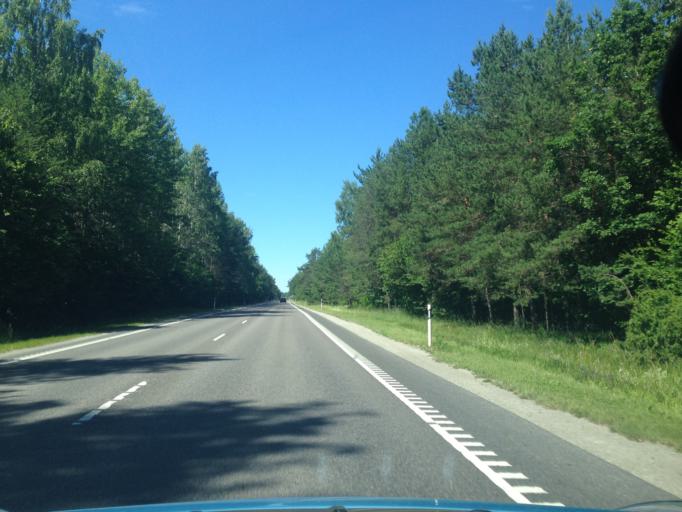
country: EE
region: Harju
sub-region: Saue linn
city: Saue
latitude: 59.3120
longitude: 24.5464
